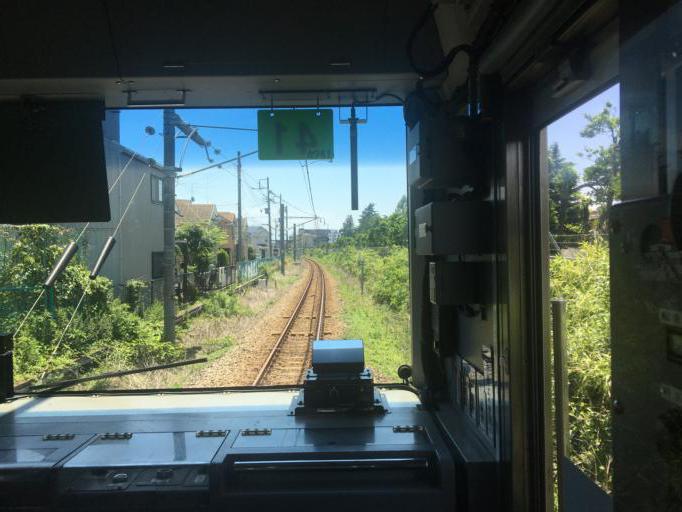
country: JP
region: Tokyo
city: Fussa
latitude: 35.7498
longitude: 139.3371
